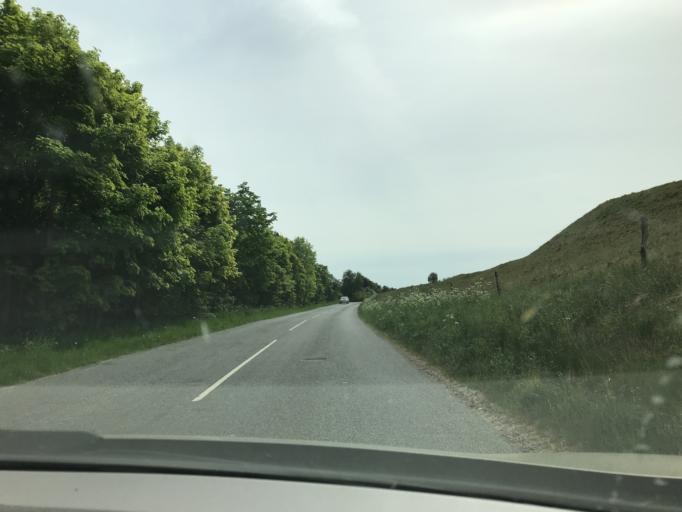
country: DK
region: Central Jutland
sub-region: Norddjurs Kommune
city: Allingabro
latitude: 56.5778
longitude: 10.3004
